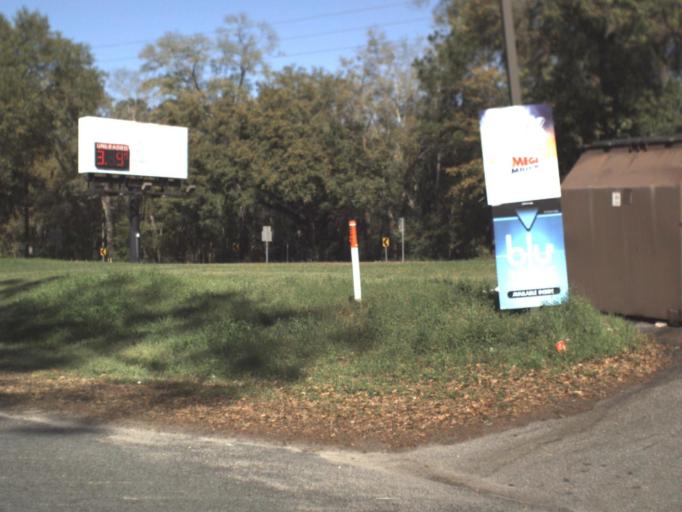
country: US
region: Florida
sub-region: Leon County
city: Tallahassee
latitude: 30.4127
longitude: -84.3081
